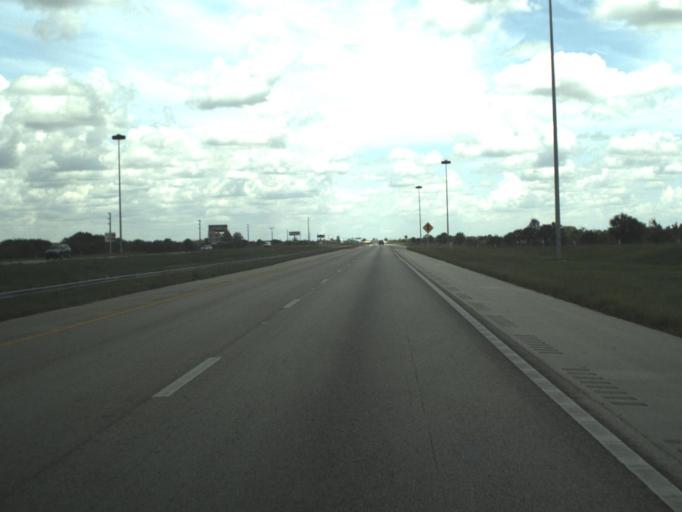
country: US
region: Florida
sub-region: Broward County
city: Weston
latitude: 26.1702
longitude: -80.8540
